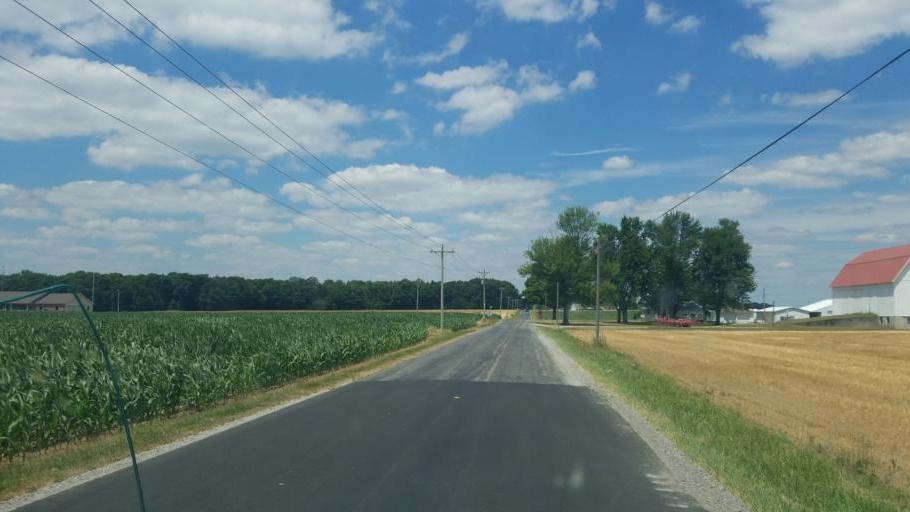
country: US
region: Ohio
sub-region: Williams County
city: Edgerton
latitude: 41.4394
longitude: -84.7103
